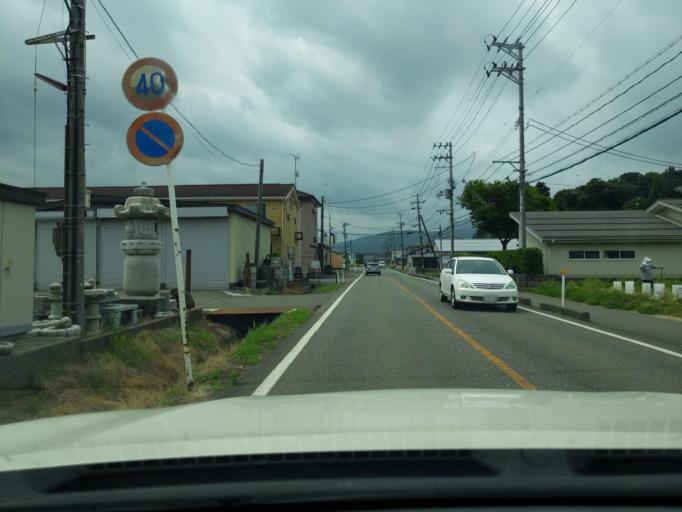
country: JP
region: Niigata
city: Kashiwazaki
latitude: 37.3477
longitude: 138.5695
